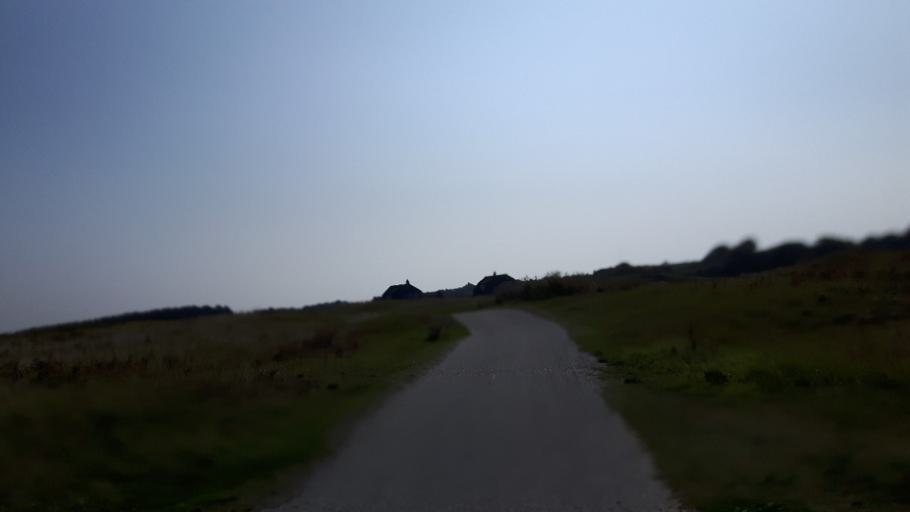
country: NL
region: Friesland
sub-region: Gemeente Ameland
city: Nes
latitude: 53.4591
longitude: 5.7976
